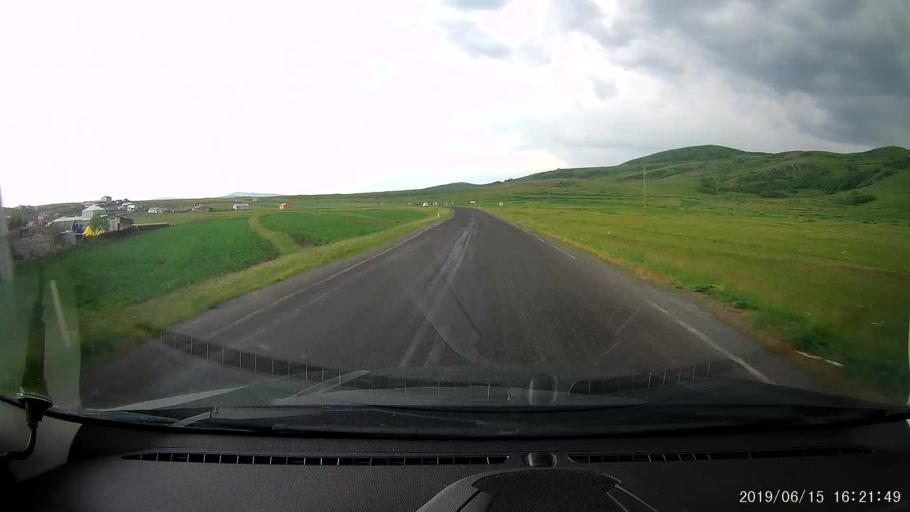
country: TR
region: Ardahan
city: Hanak
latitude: 41.1948
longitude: 42.8457
